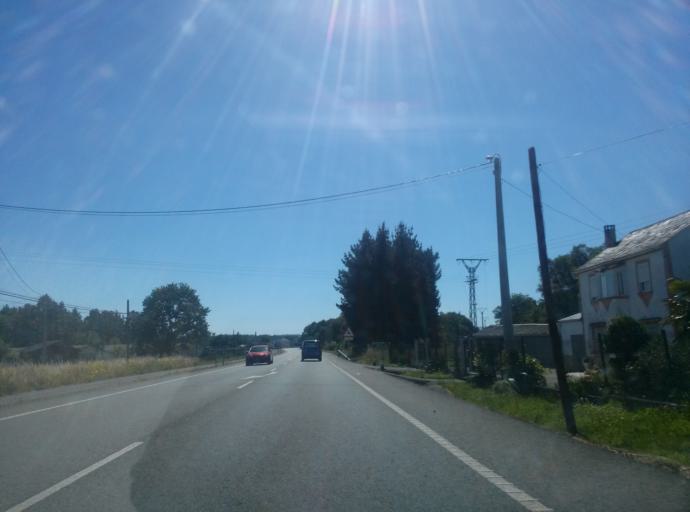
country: ES
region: Galicia
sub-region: Provincia de Lugo
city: Mos
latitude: 43.1195
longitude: -7.5709
